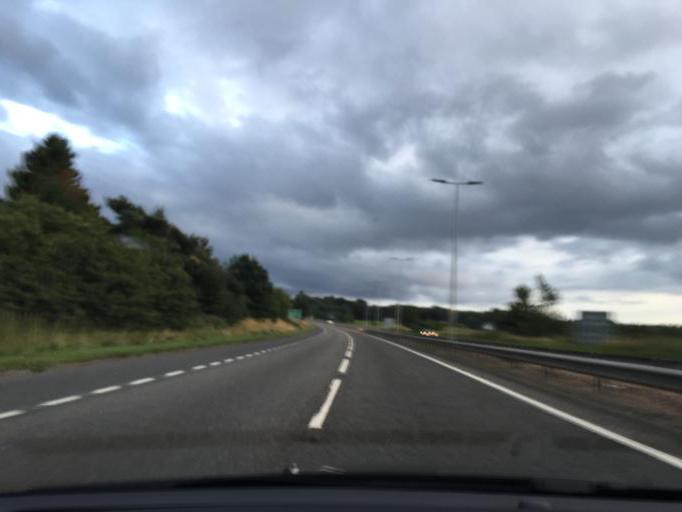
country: GB
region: Scotland
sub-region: Highland
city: Inverness
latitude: 57.4711
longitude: -4.1836
